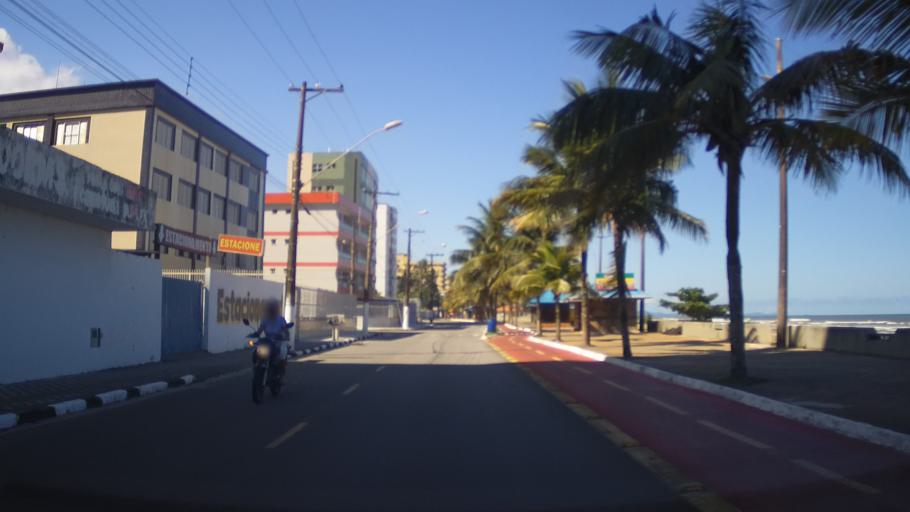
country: BR
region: Sao Paulo
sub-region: Mongagua
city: Mongagua
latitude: -24.0988
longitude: -46.6256
